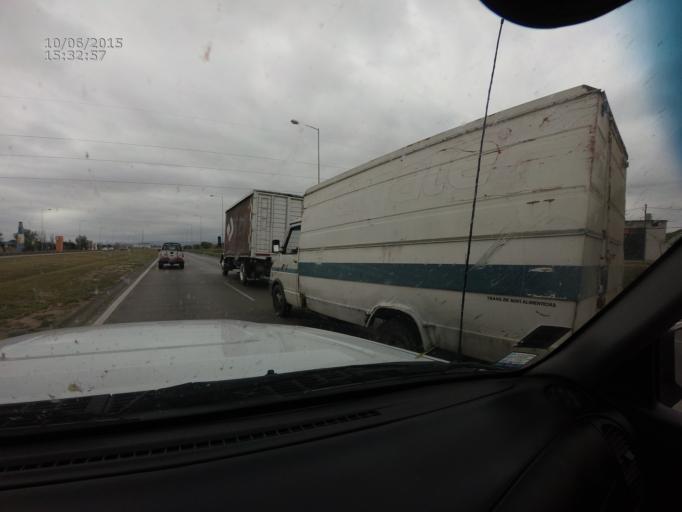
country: AR
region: Cordoba
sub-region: Departamento de Capital
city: Cordoba
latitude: -31.3614
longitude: -64.1531
